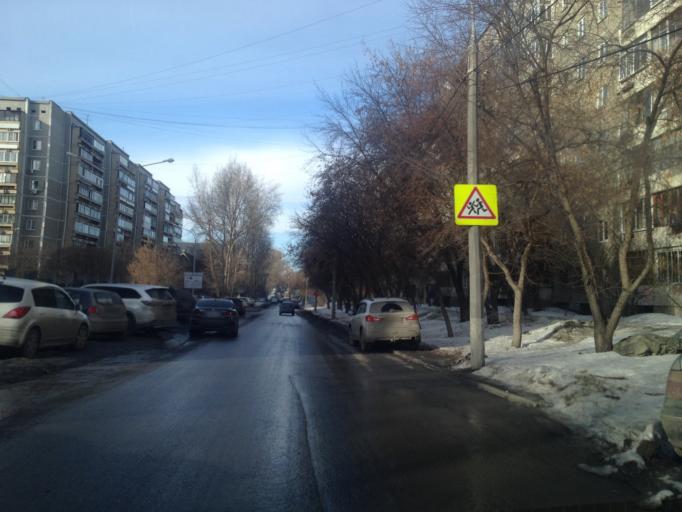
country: RU
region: Sverdlovsk
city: Yekaterinburg
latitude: 56.8329
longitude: 60.6290
